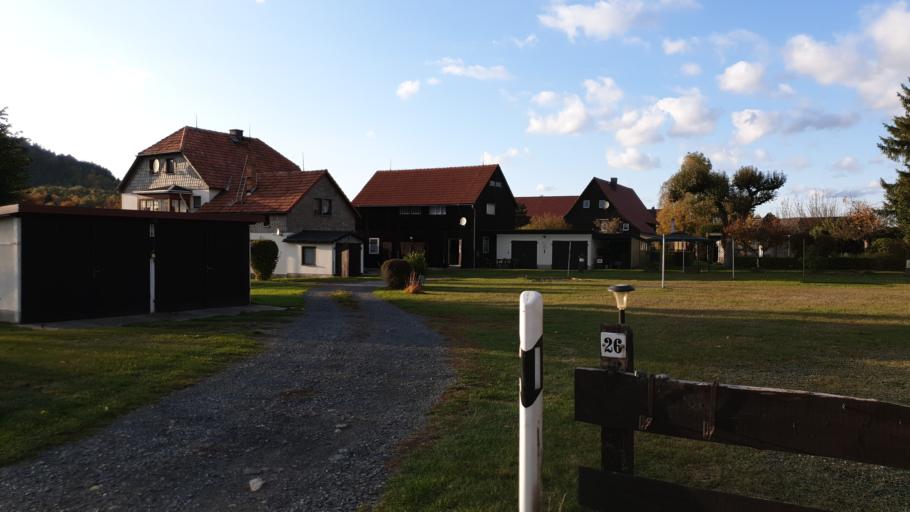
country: DE
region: Saxony
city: Bad Schandau
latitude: 50.9057
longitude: 14.1475
